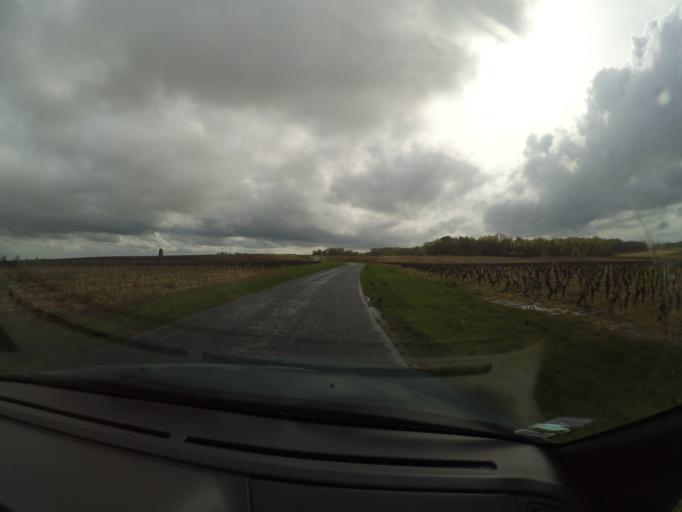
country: FR
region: Pays de la Loire
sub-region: Departement de la Loire-Atlantique
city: Monnieres
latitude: 47.1240
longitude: -1.3553
